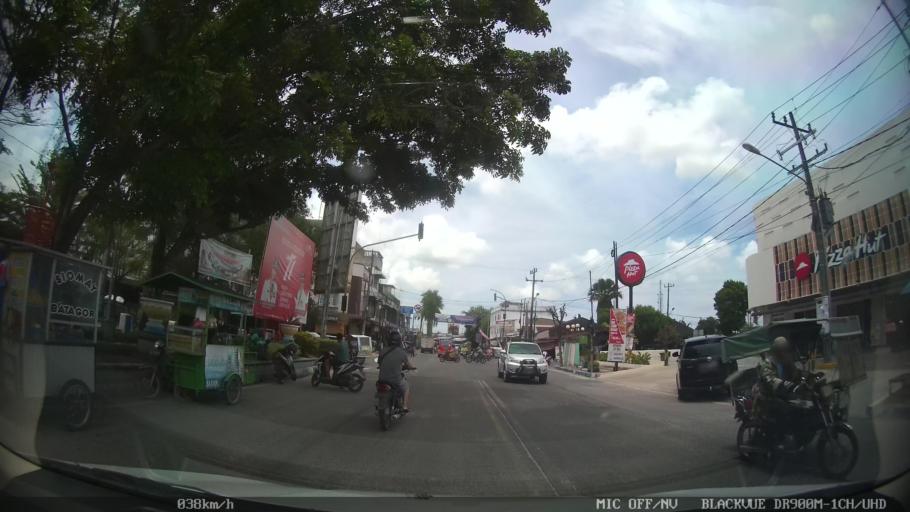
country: ID
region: North Sumatra
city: Percut
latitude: 3.5600
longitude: 98.8797
